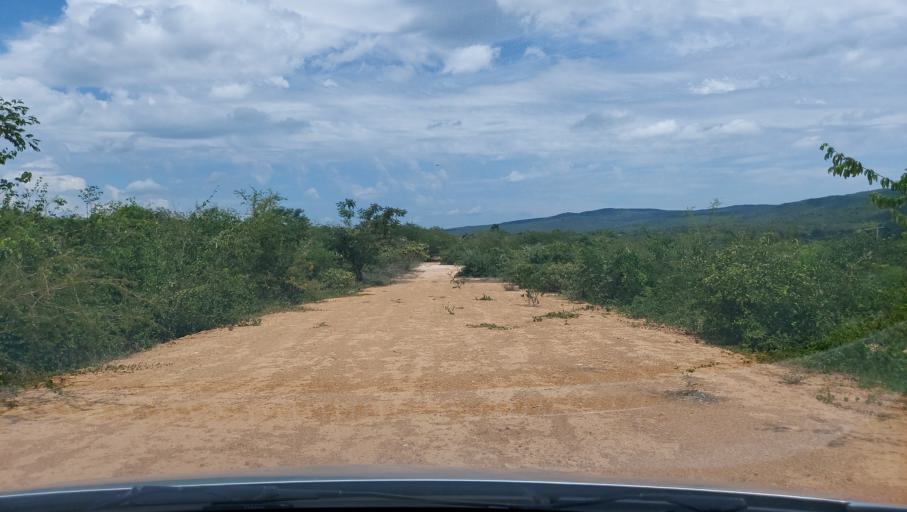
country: BR
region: Bahia
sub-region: Oliveira Dos Brejinhos
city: Beira Rio
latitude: -12.0131
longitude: -42.6299
